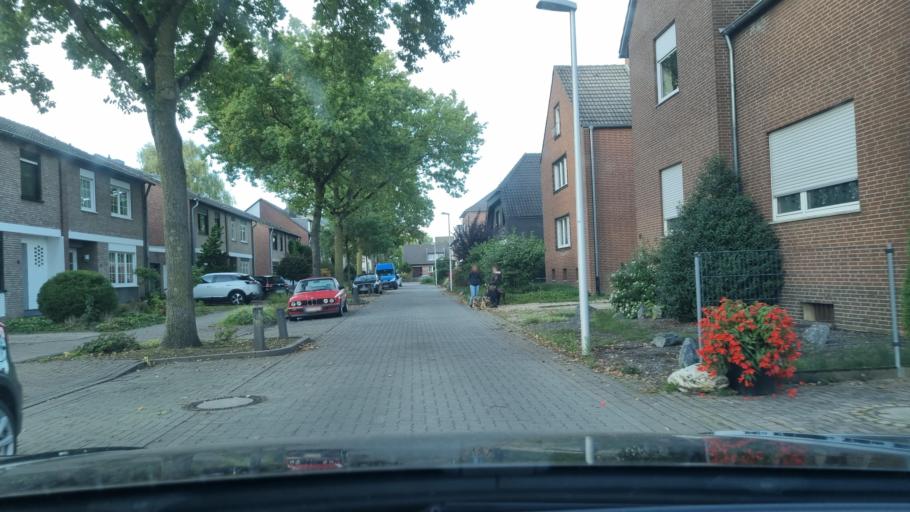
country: DE
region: North Rhine-Westphalia
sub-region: Regierungsbezirk Dusseldorf
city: Kleve
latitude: 51.7841
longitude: 6.1423
